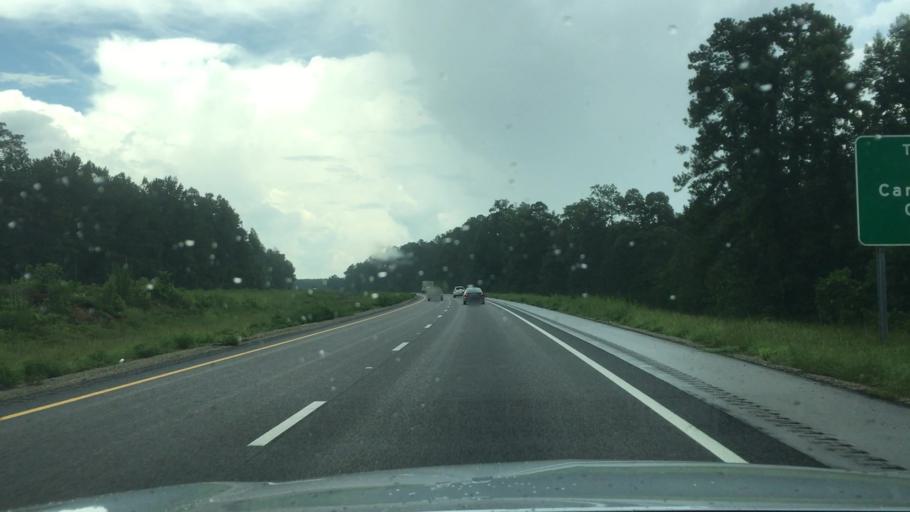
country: US
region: Mississippi
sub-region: Forrest County
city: Hattiesburg
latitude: 31.2266
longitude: -89.3235
